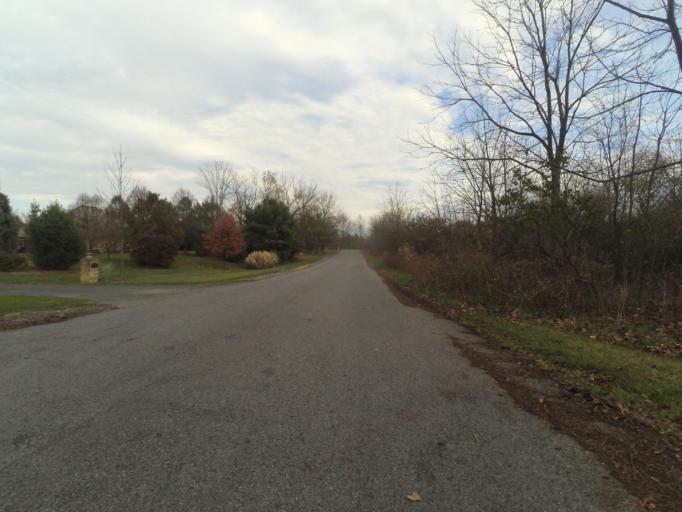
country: US
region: Pennsylvania
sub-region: Centre County
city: Boalsburg
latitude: 40.7794
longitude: -77.8109
